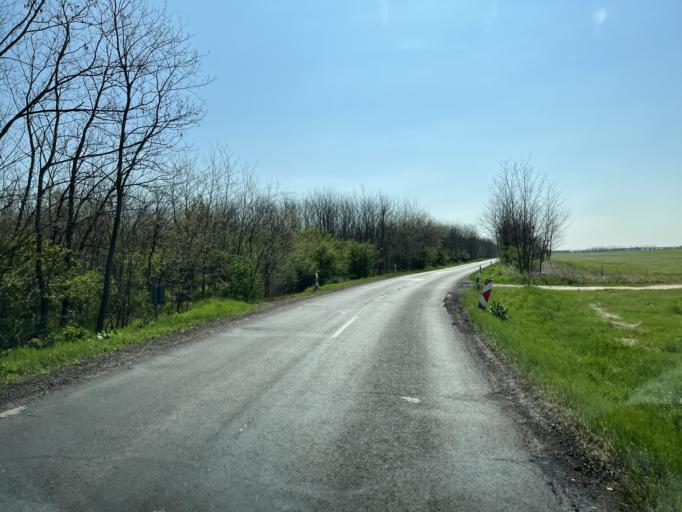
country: HU
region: Pest
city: Felsopakony
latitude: 47.3356
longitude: 19.2914
